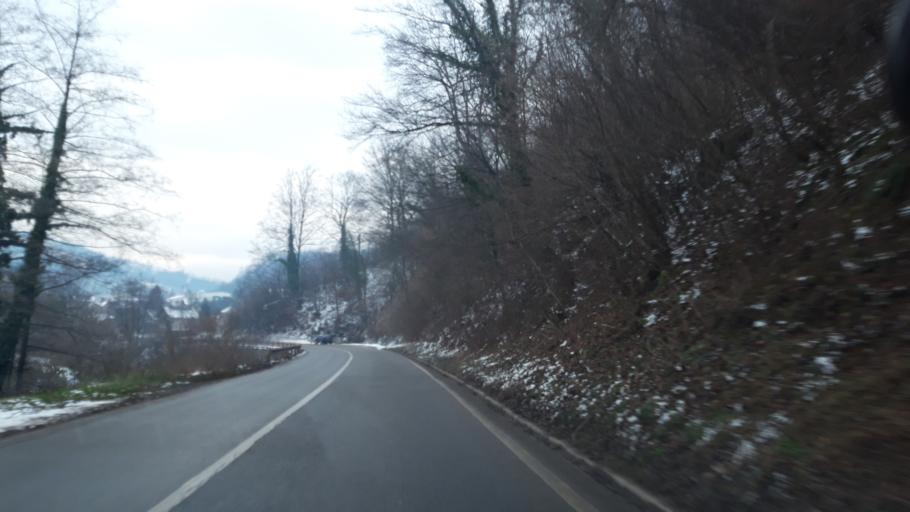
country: BA
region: Republika Srpska
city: Milici
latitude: 44.1895
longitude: 19.0708
